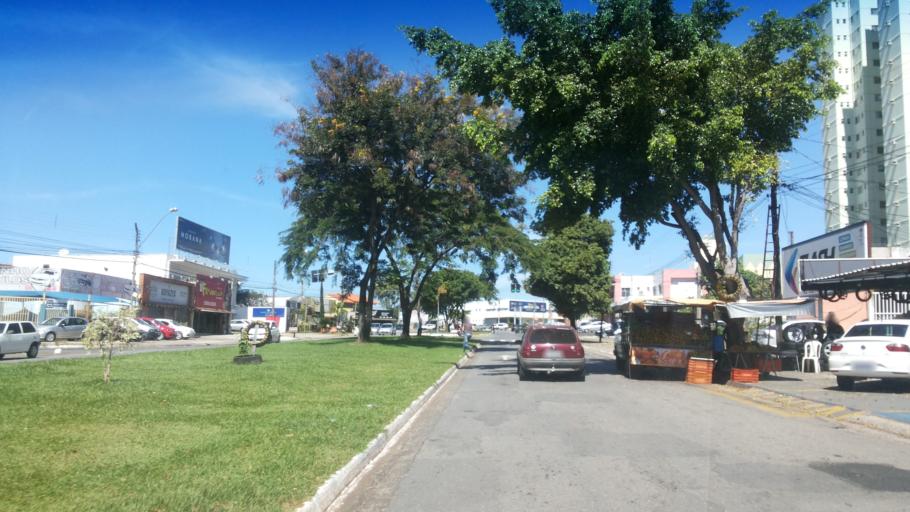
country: BR
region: Goias
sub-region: Goiania
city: Goiania
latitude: -16.7182
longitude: -49.2586
